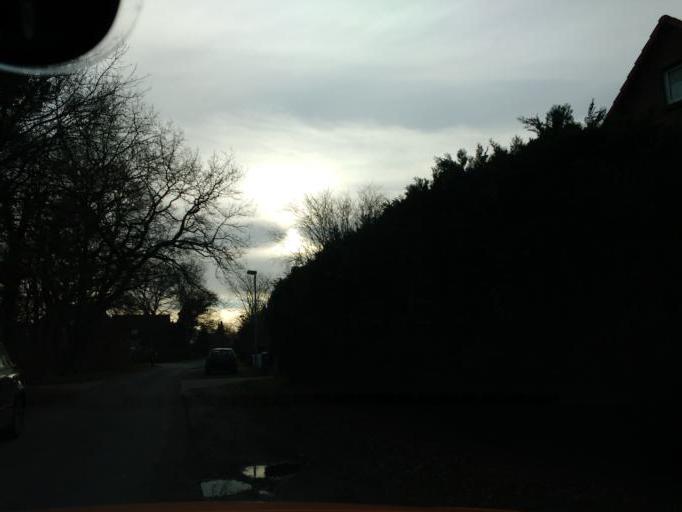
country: DE
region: Lower Saxony
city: Hude
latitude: 53.0967
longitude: 8.4555
